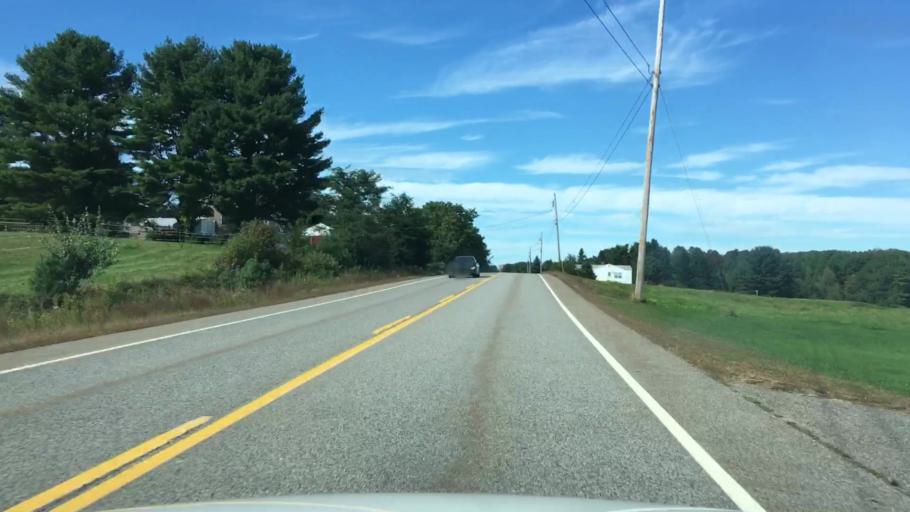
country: US
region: Maine
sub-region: Cumberland County
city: Westbrook
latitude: 43.6620
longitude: -70.4042
